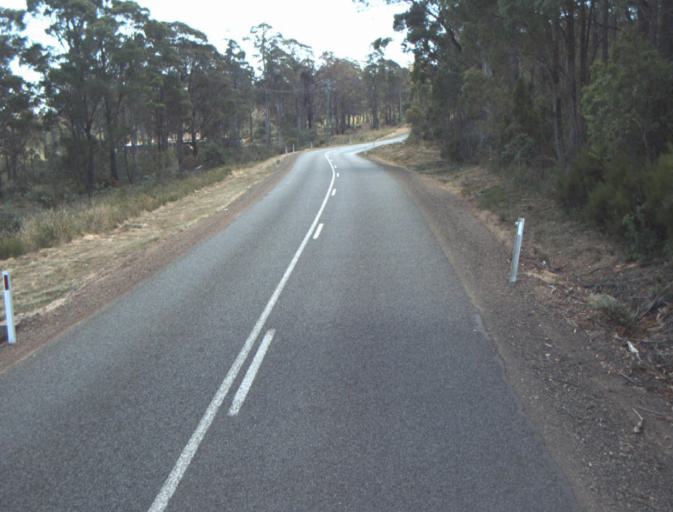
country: AU
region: Tasmania
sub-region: Launceston
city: Mayfield
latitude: -41.3223
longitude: 147.1363
